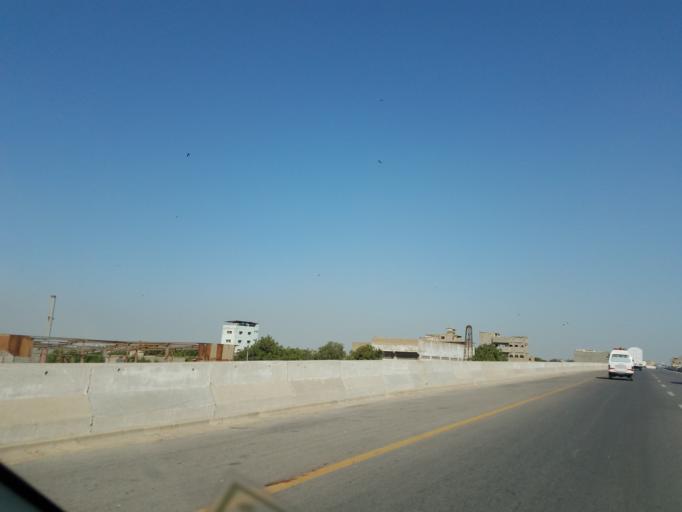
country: PK
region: Sindh
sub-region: Karachi District
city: Karachi
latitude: 24.8821
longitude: 67.0020
